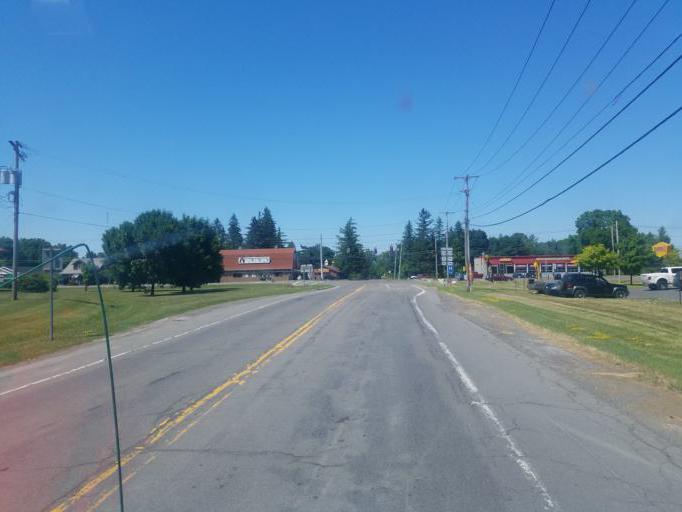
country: US
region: New York
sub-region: Ontario County
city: Geneva
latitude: 42.8560
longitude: -77.0140
